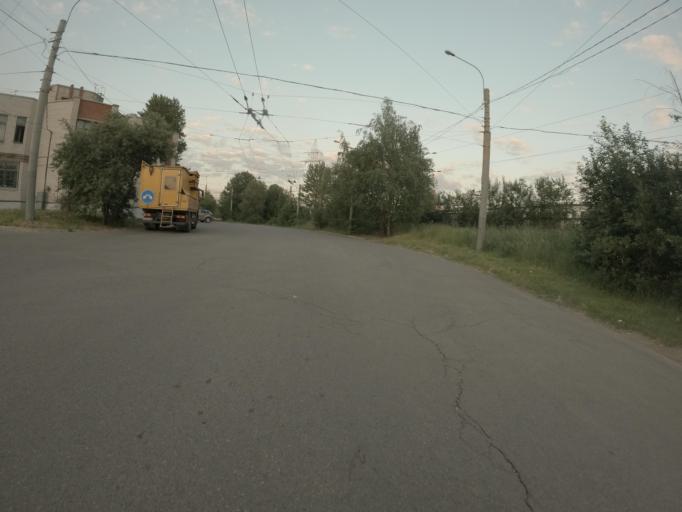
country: RU
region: St.-Petersburg
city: Avtovo
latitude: 59.8762
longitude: 30.2785
